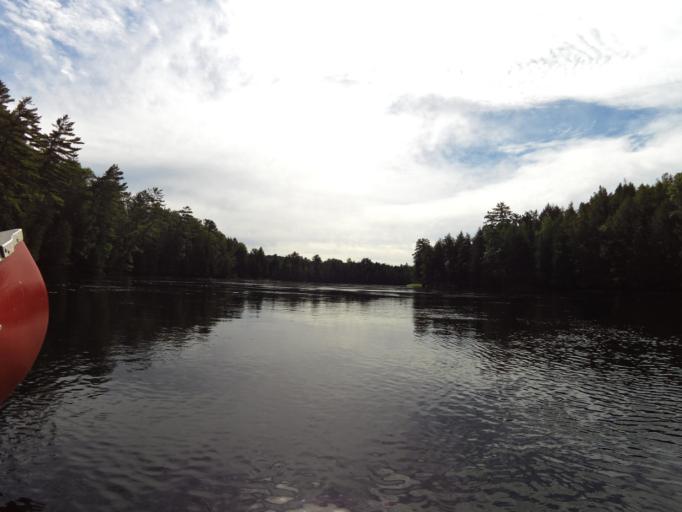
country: CA
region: Quebec
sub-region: Outaouais
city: Wakefield
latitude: 45.7786
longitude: -75.9421
